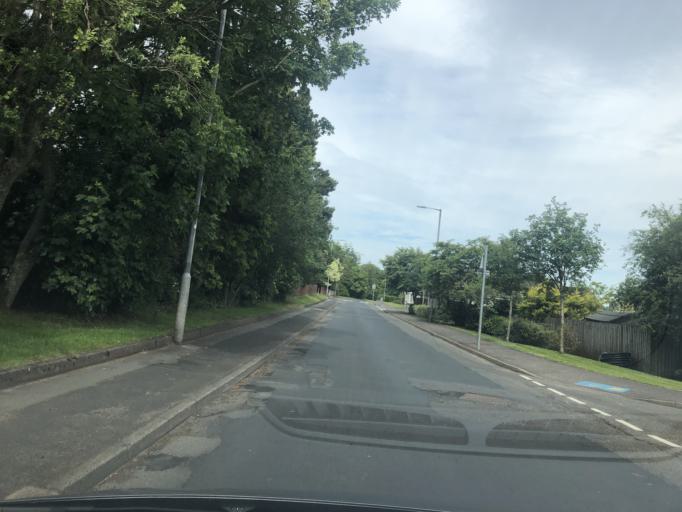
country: GB
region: Scotland
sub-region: The Scottish Borders
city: West Linton
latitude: 55.7545
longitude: -3.3510
